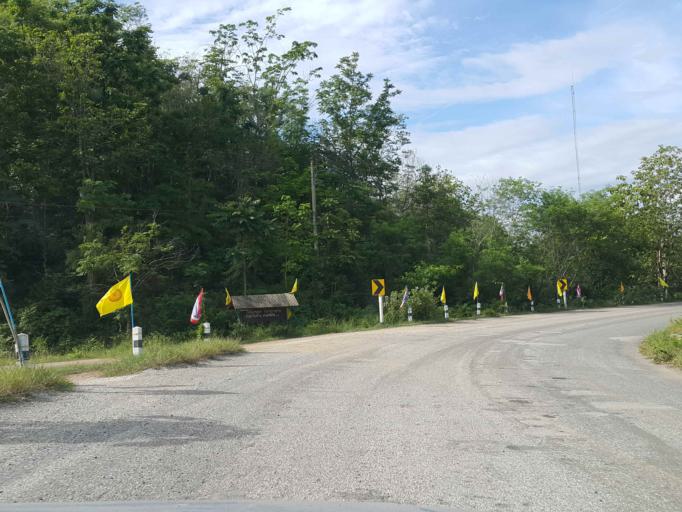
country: TH
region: Sukhothai
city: Thung Saliam
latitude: 17.2649
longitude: 99.5349
